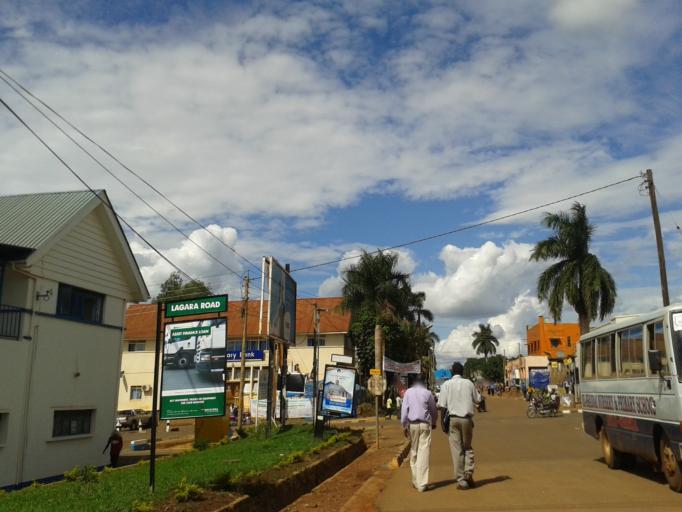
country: UG
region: Northern Region
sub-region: Gulu District
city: Gulu
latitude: 2.7735
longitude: 32.2971
